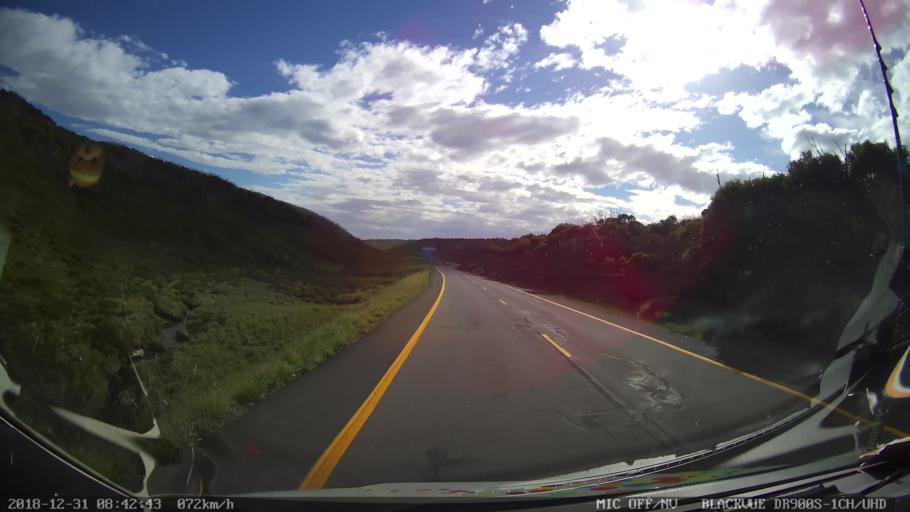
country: AU
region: New South Wales
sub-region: Snowy River
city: Jindabyne
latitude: -36.3927
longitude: 148.4361
